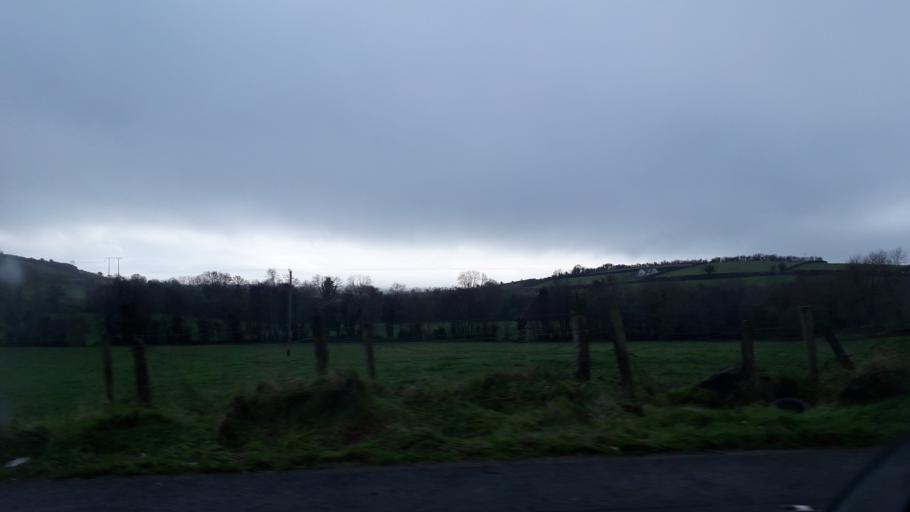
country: IE
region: Ulster
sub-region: County Donegal
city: Raphoe
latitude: 54.9367
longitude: -7.6129
